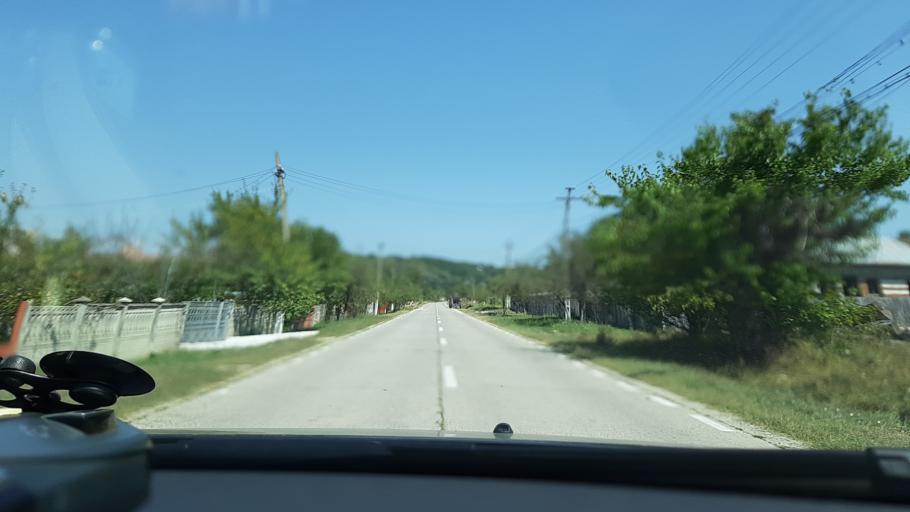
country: RO
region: Gorj
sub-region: Comuna Logresti-Mosteni
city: Logresti Mosteni
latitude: 44.8961
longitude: 23.7304
